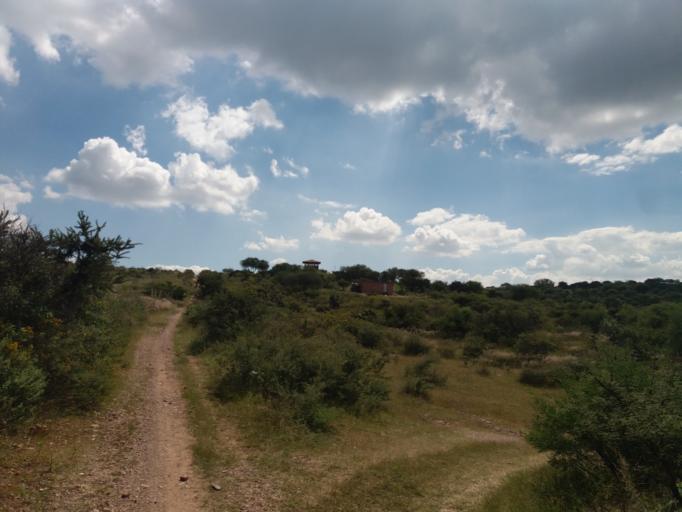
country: MX
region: Aguascalientes
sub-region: Aguascalientes
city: San Sebastian [Fraccionamiento]
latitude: 21.8033
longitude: -102.2425
